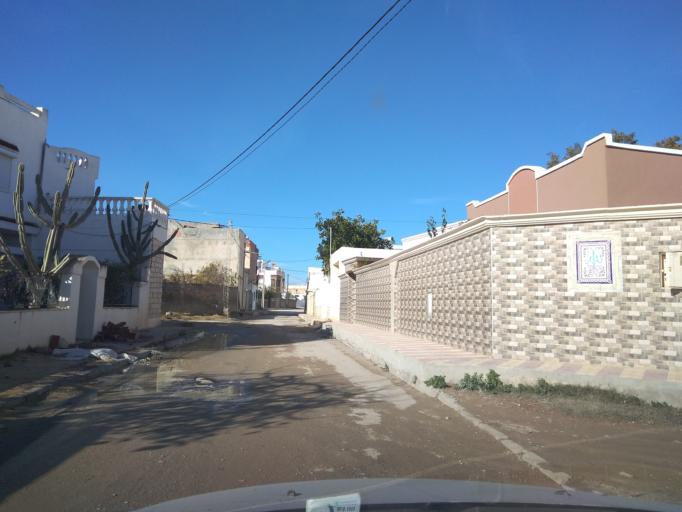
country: TN
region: Ariana
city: Qal'at al Andalus
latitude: 37.0585
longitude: 10.1216
